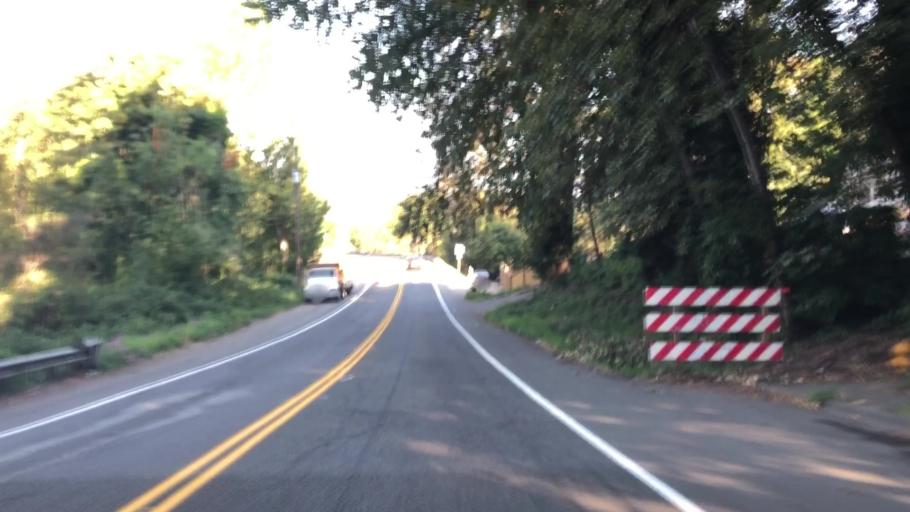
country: US
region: Washington
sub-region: King County
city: Tukwila
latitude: 47.4884
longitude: -122.2620
